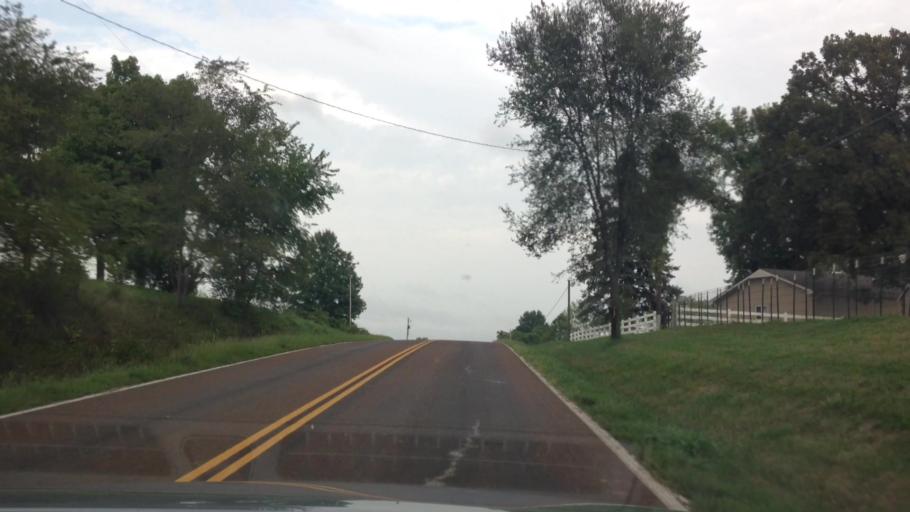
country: US
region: Missouri
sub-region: Clay County
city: Smithville
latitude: 39.4050
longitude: -94.6229
